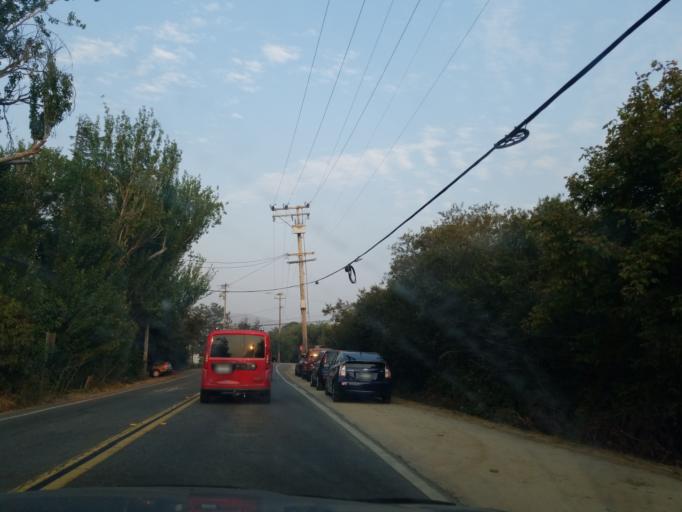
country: US
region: California
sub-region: Marin County
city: Inverness
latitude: 38.0643
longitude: -122.8063
